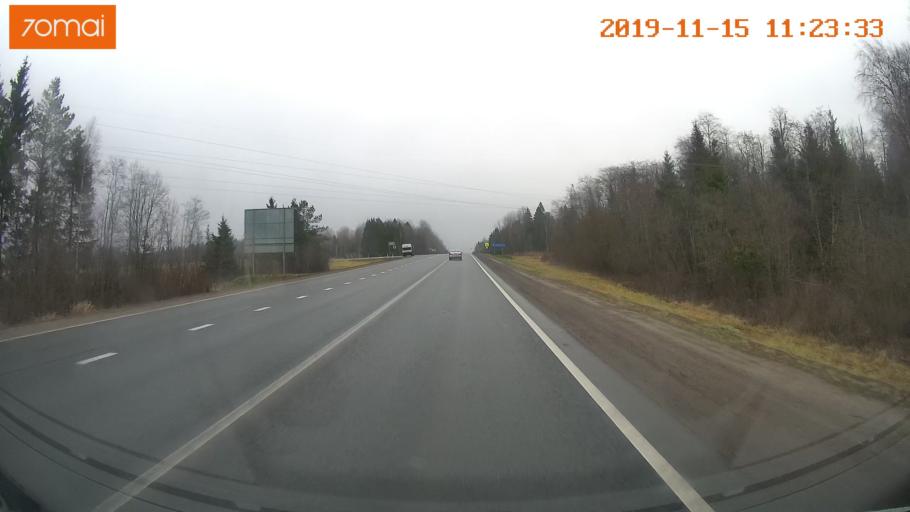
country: RU
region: Vologda
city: Molochnoye
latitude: 59.1521
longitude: 39.3847
